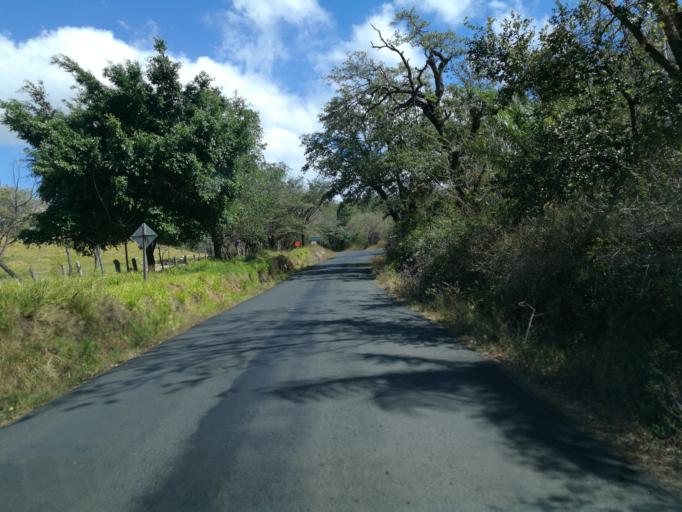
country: CR
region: Guanacaste
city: Liberia
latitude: 10.7465
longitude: -85.3816
